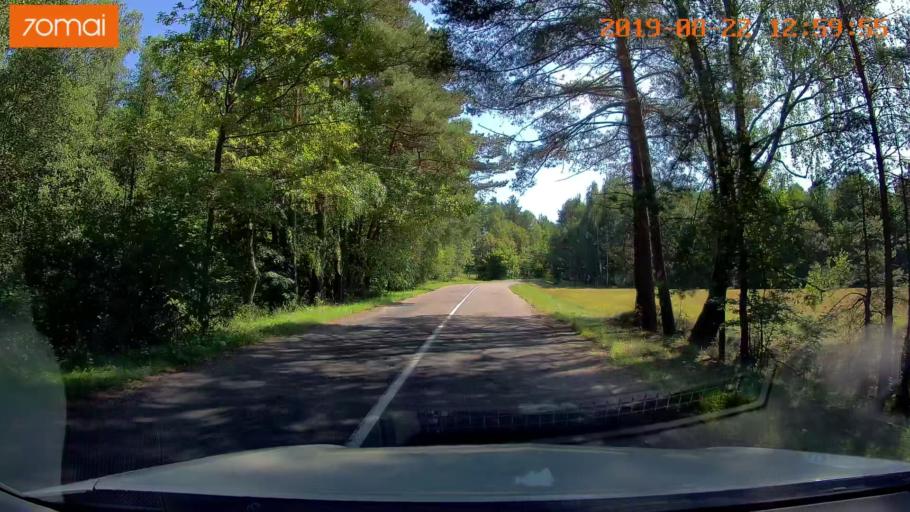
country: BY
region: Minsk
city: Prawdzinski
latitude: 53.4207
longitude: 27.8009
